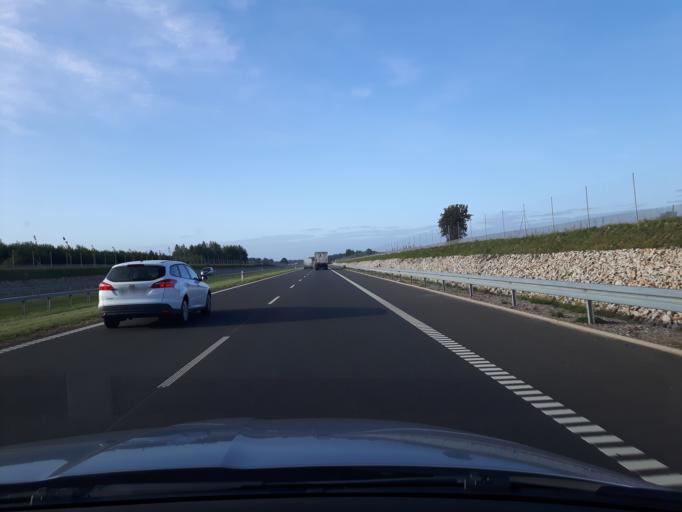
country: PL
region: Masovian Voivodeship
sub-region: Powiat radomski
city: Zakrzew
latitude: 51.4584
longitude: 21.0430
